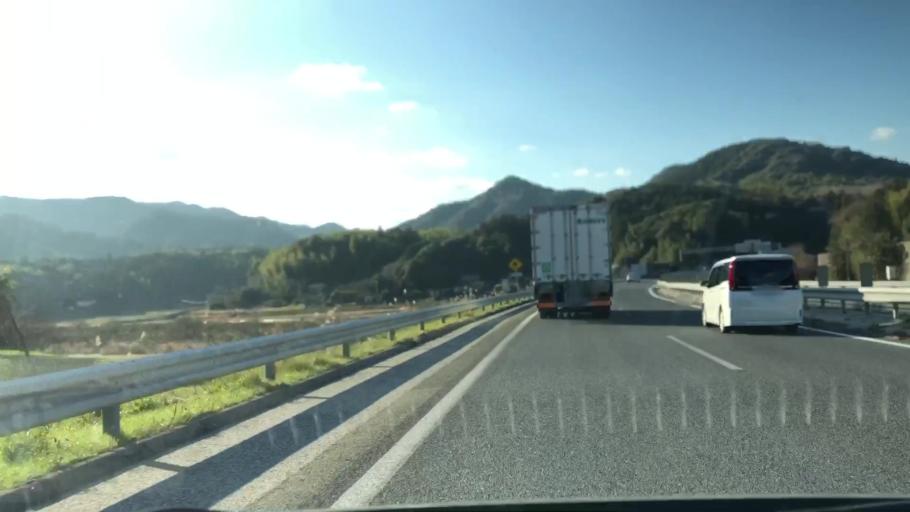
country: JP
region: Yamaguchi
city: Ogori-shimogo
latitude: 34.1727
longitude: 131.3149
